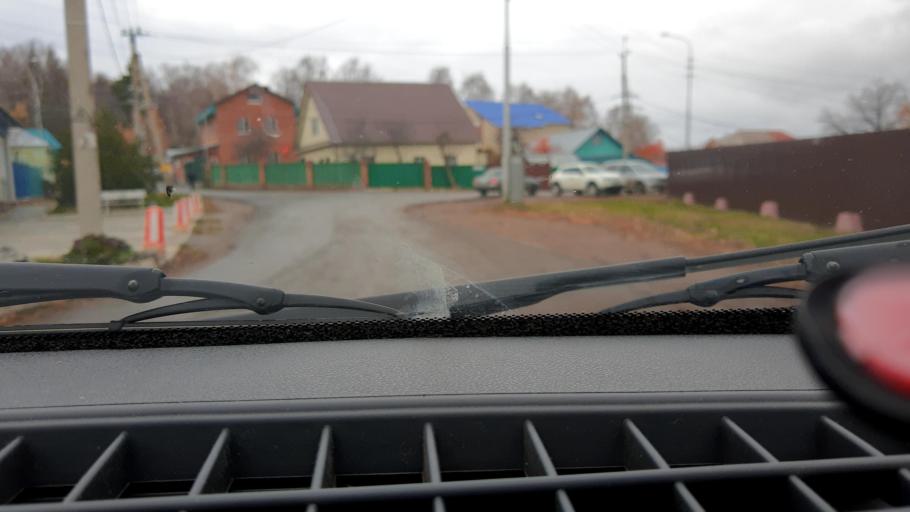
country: RU
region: Bashkortostan
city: Ufa
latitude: 54.7237
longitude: 55.9223
